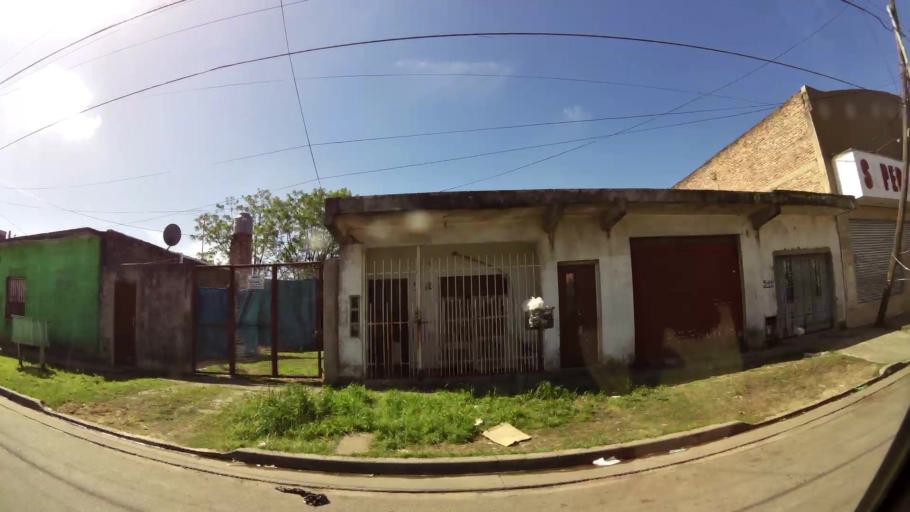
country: AR
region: Buenos Aires
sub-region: Partido de Quilmes
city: Quilmes
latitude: -34.8003
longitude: -58.2693
